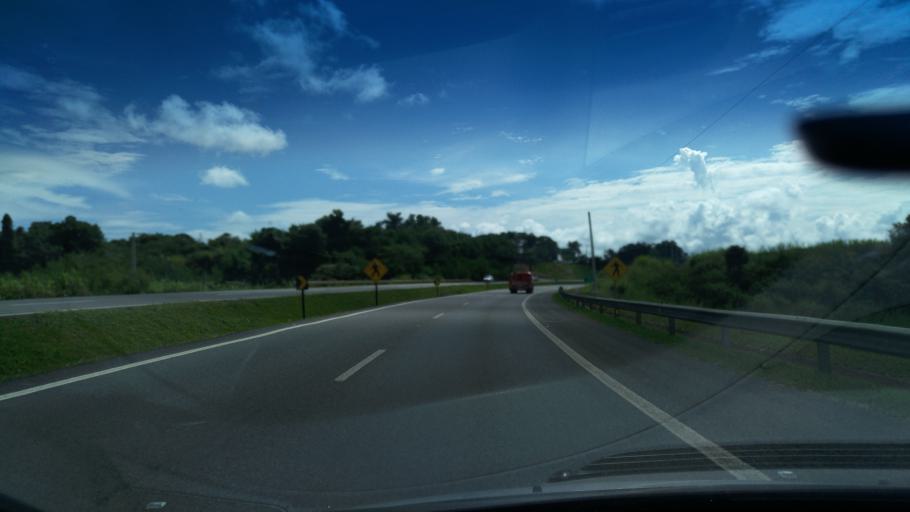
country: BR
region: Sao Paulo
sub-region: Santo Antonio Do Jardim
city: Espirito Santo do Pinhal
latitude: -22.2010
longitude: -46.7777
